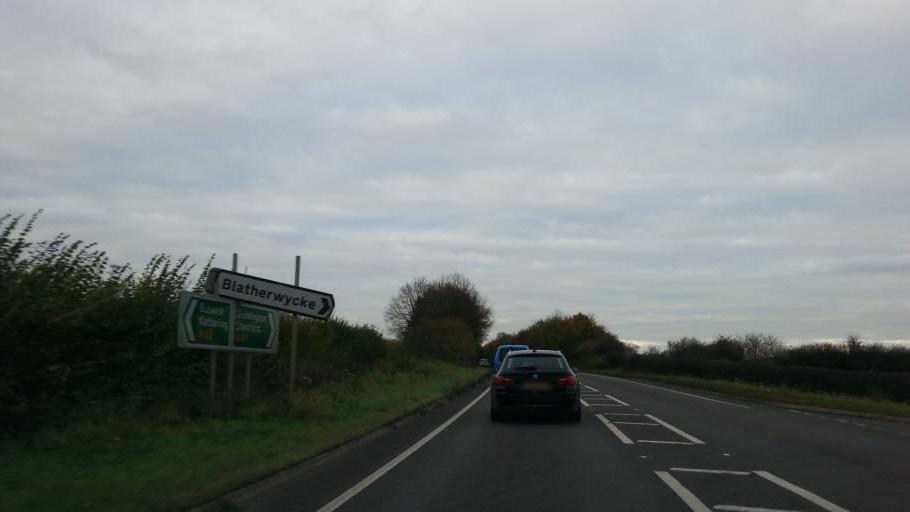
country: GB
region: England
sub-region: District of Rutland
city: South Luffenham
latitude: 52.5581
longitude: -0.5751
